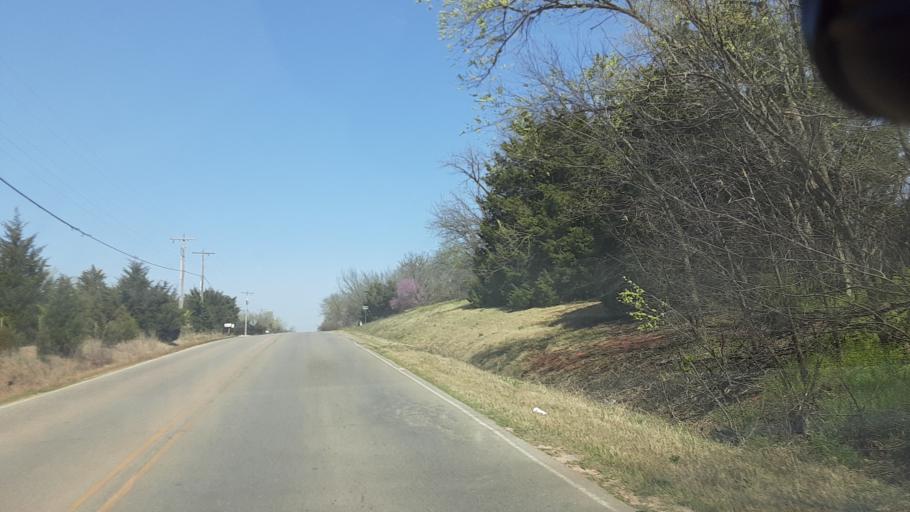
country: US
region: Oklahoma
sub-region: Oklahoma County
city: Edmond
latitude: 35.7415
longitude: -97.4784
